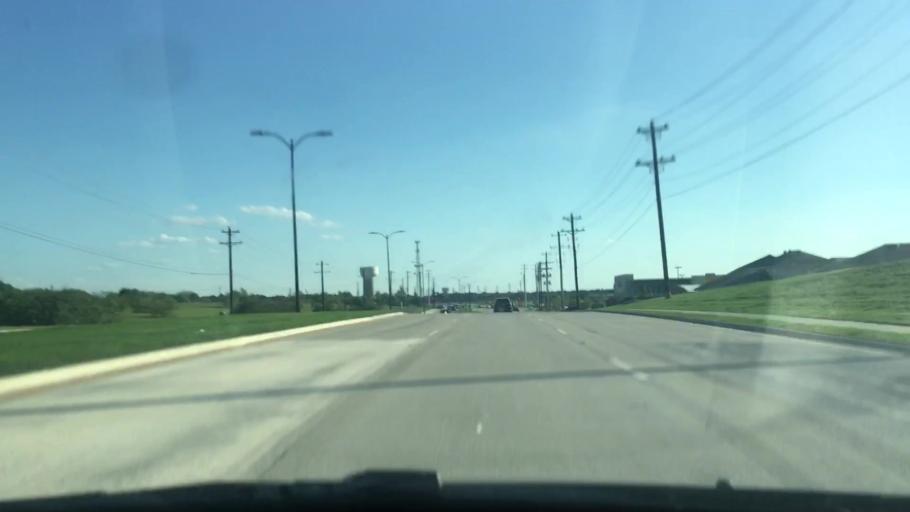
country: US
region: Texas
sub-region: Denton County
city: Little Elm
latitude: 33.1957
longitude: -96.8842
